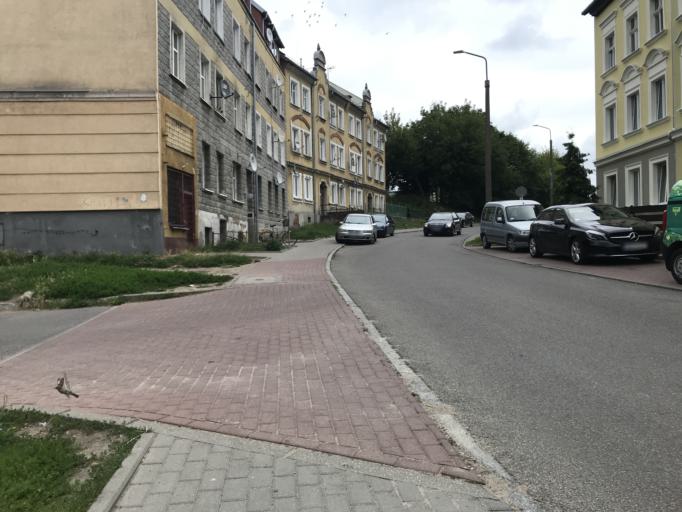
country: PL
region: Warmian-Masurian Voivodeship
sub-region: Powiat elblaski
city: Elblag
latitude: 54.1710
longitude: 19.3989
